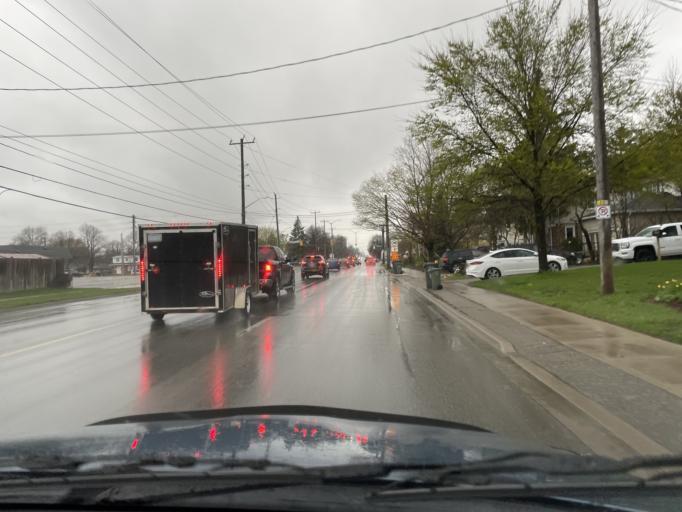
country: CA
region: Ontario
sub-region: Wellington County
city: Guelph
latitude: 43.5704
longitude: -80.2497
